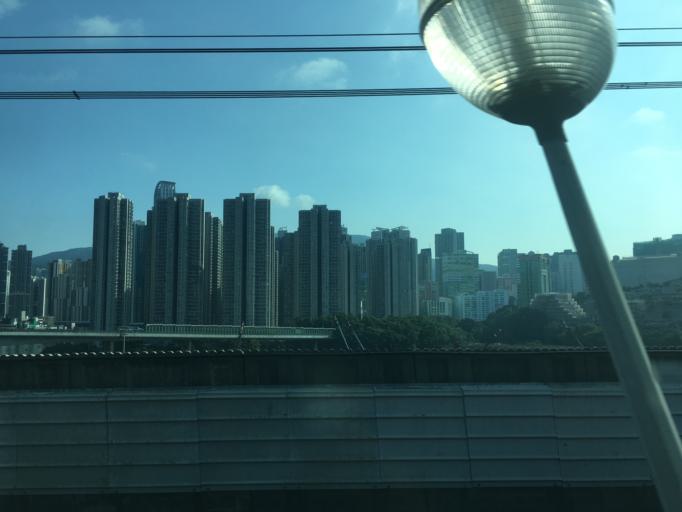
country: HK
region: Tsuen Wan
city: Tsuen Wan
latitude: 22.3570
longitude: 114.1120
